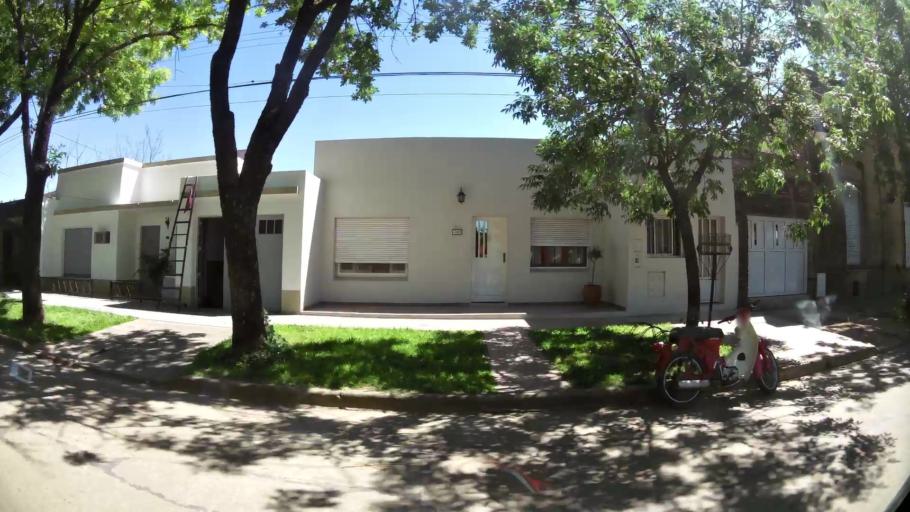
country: AR
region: Santa Fe
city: Esperanza
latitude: -31.4375
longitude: -60.9282
